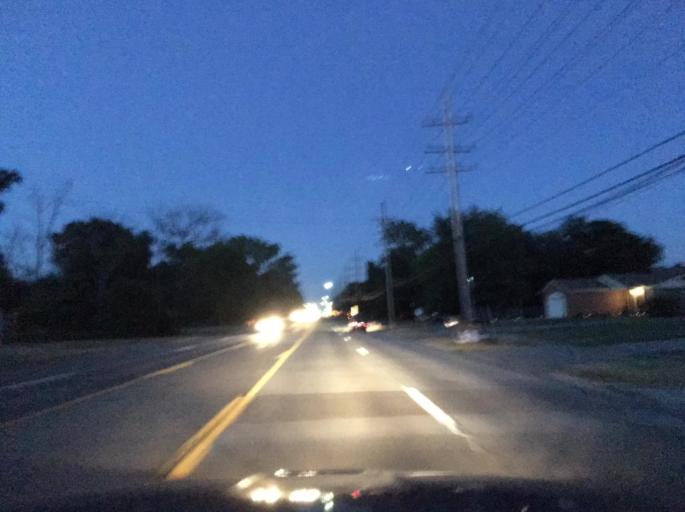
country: US
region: Michigan
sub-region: Macomb County
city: Fraser
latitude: 42.5386
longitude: -82.9611
